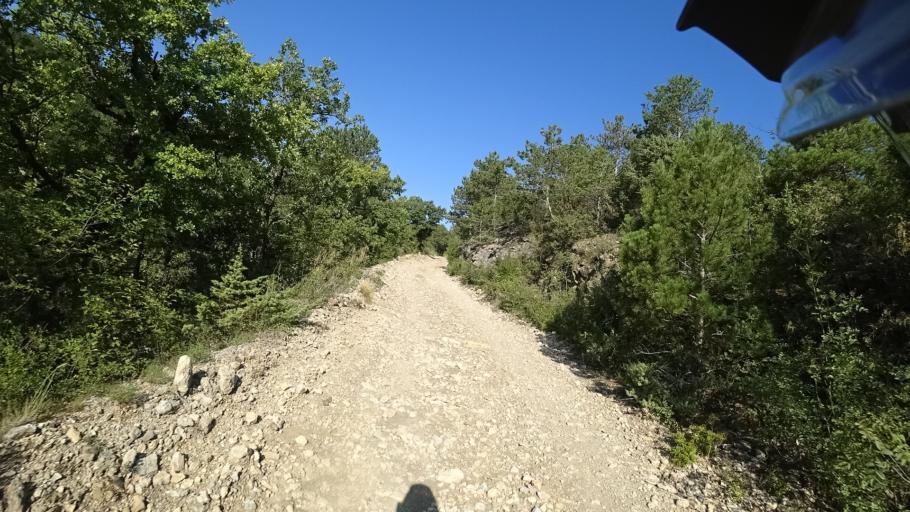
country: HR
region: Sibensko-Kniniska
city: Knin
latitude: 44.1342
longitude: 16.1808
